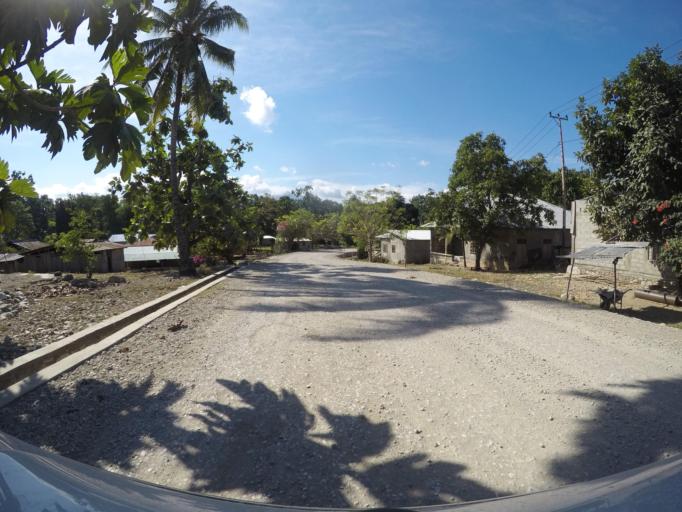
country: TL
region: Viqueque
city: Viqueque
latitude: -8.8404
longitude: 126.5165
